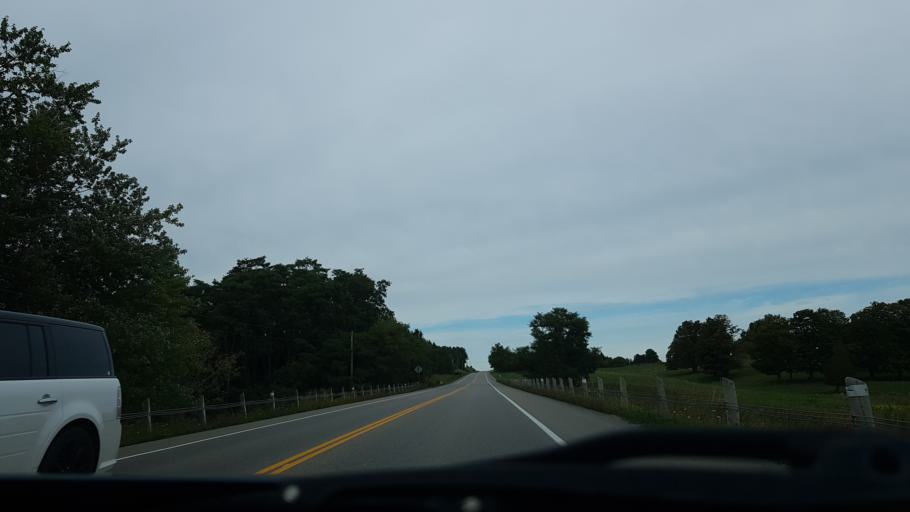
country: CA
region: Ontario
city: Orangeville
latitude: 44.0278
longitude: -80.0056
